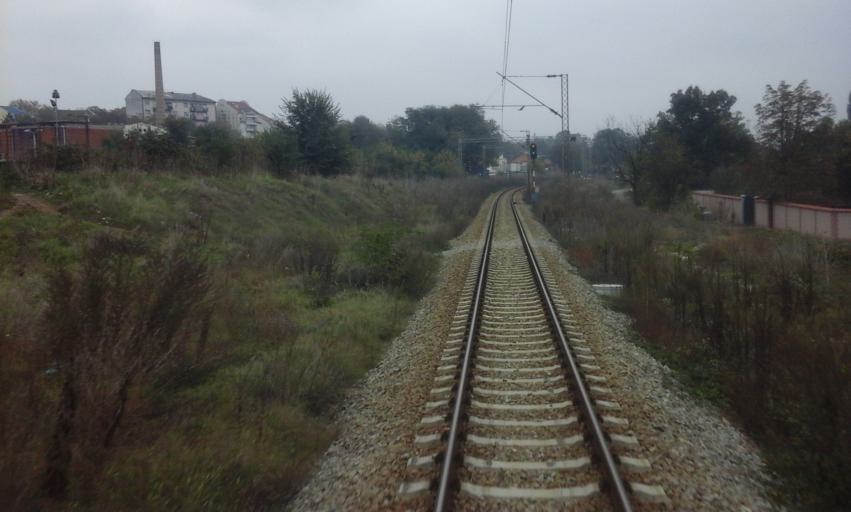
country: RS
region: Central Serbia
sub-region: Belgrade
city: Mladenovac
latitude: 44.4450
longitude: 20.6862
